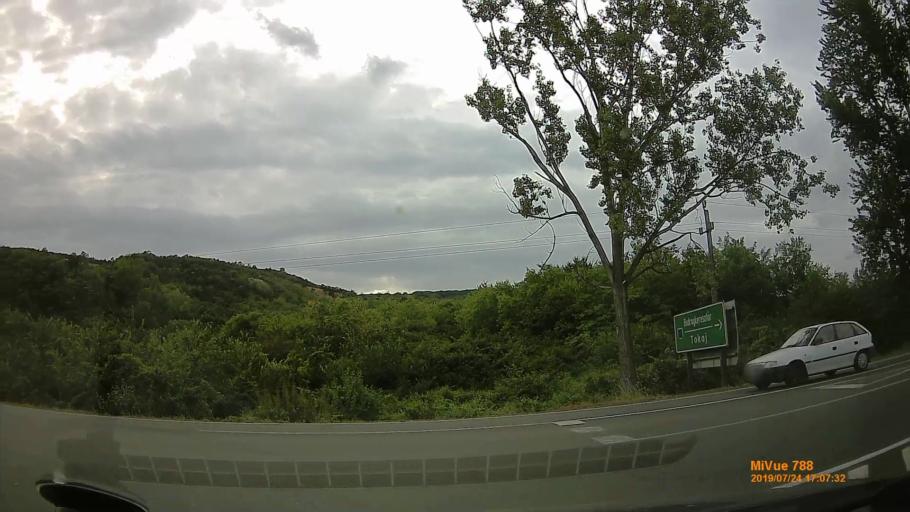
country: HU
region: Borsod-Abauj-Zemplen
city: Tarcal
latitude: 48.1752
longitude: 21.3469
